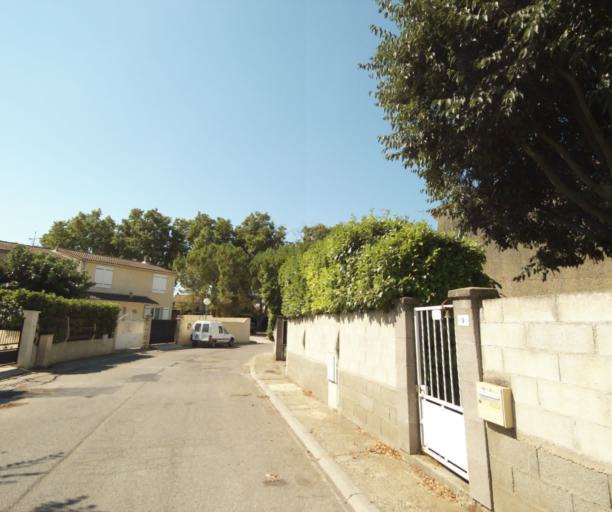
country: FR
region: Languedoc-Roussillon
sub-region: Departement de l'Herault
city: Marsillargues
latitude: 43.6637
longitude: 4.1689
